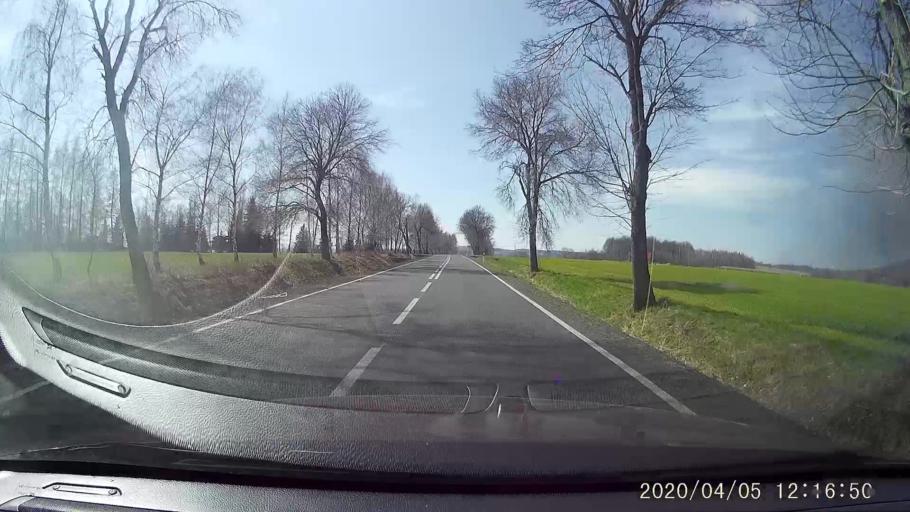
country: PL
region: Lower Silesian Voivodeship
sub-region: Powiat lwowecki
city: Gryfow Slaski
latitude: 51.0133
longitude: 15.3809
